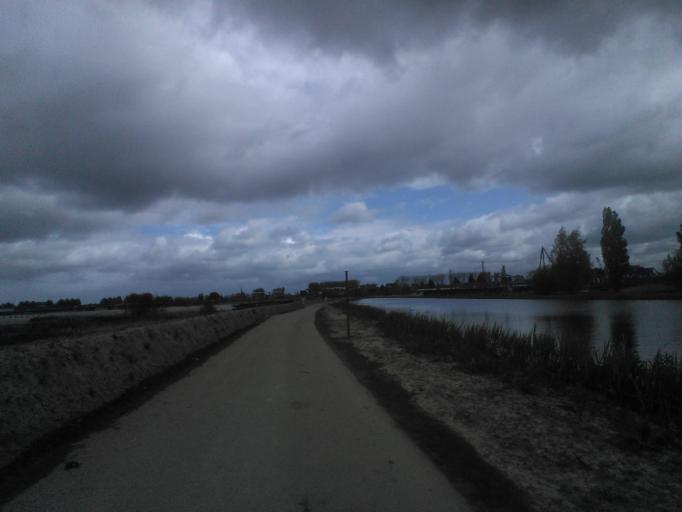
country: NL
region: South Holland
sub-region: Gemeente Gouda
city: Gouda
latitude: 51.9985
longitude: 4.6845
